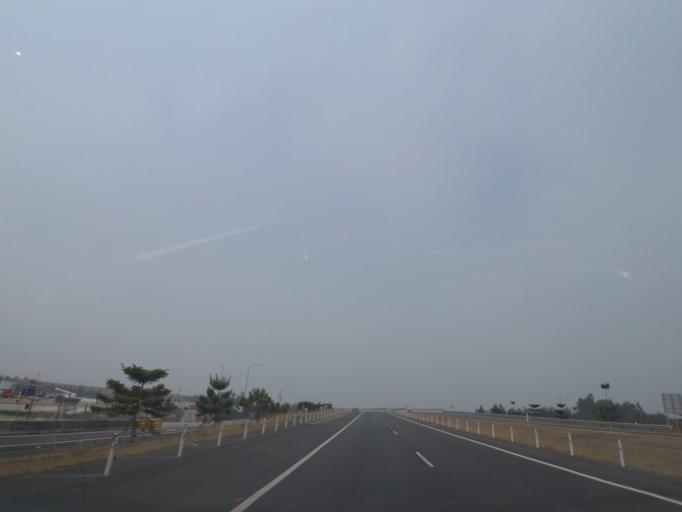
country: AU
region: New South Wales
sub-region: Ballina
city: Ballina
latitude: -28.8623
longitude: 153.5167
